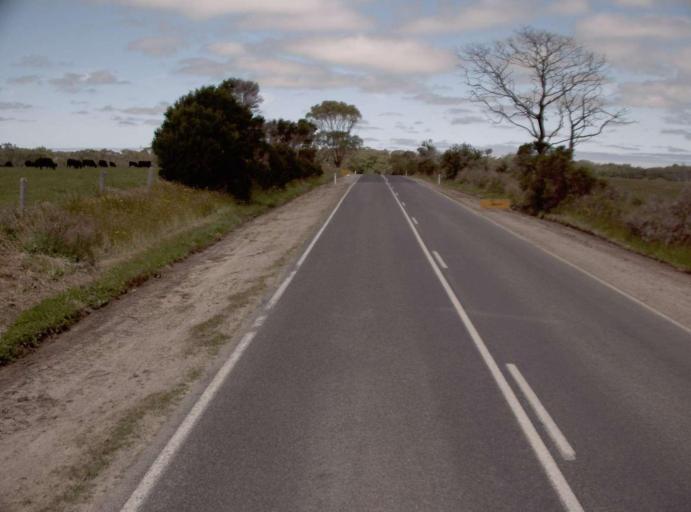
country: AU
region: Victoria
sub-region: Bass Coast
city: North Wonthaggi
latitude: -38.6420
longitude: 146.0106
